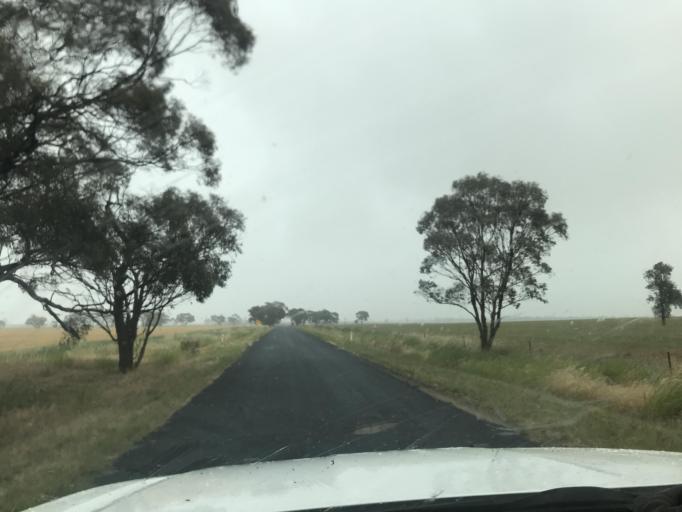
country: AU
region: South Australia
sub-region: Tatiara
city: Bordertown
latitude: -36.3135
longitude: 141.1491
